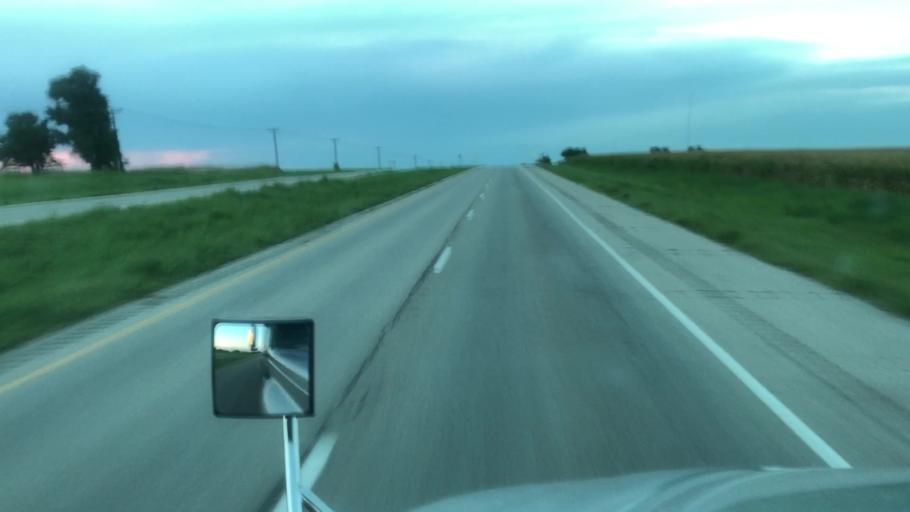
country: US
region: Oklahoma
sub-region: Kay County
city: Newkirk
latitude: 36.8008
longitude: -97.0672
